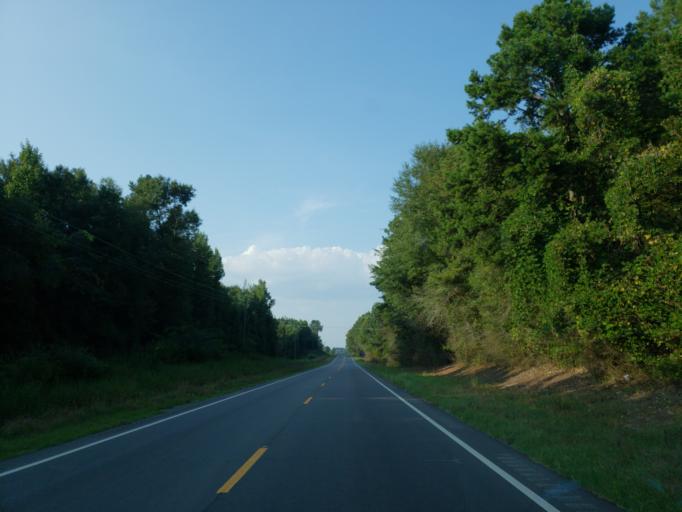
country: US
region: Alabama
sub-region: Greene County
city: Eutaw
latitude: 32.8875
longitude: -87.8649
